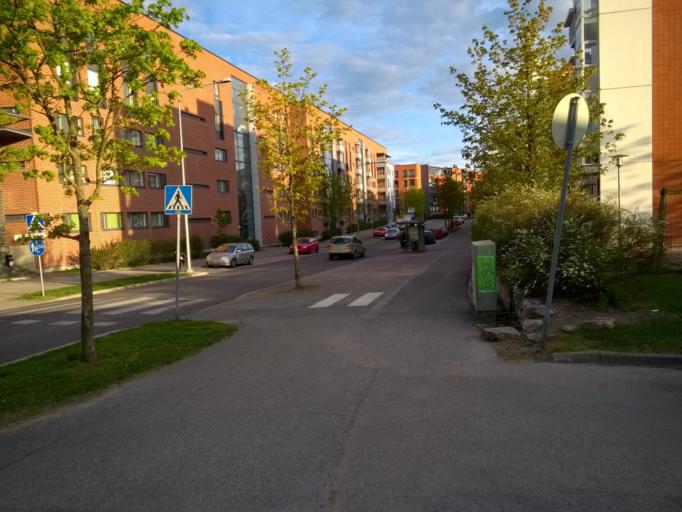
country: FI
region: Uusimaa
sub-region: Helsinki
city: Vantaa
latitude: 60.2334
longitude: 25.0307
